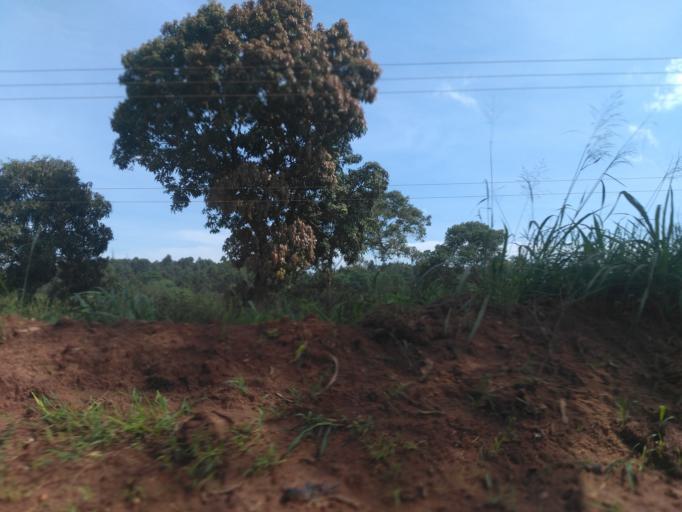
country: UG
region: Central Region
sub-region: Wakiso District
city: Kireka
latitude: 0.4427
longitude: 32.5862
